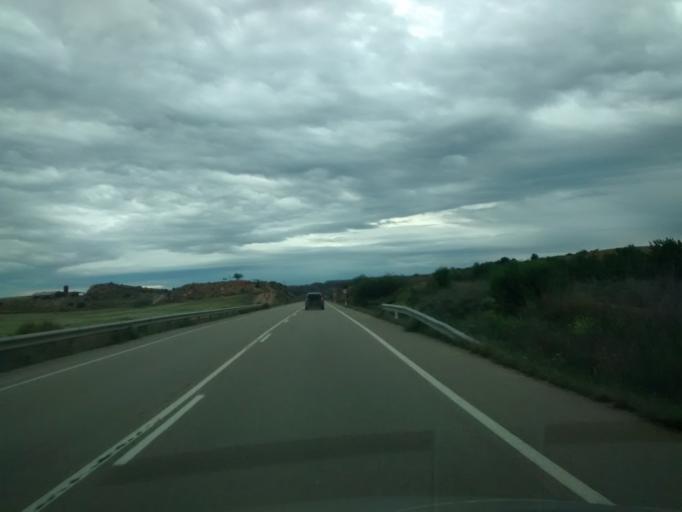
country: ES
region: Aragon
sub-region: Provincia de Zaragoza
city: Caspe
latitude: 41.1825
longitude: 0.0494
